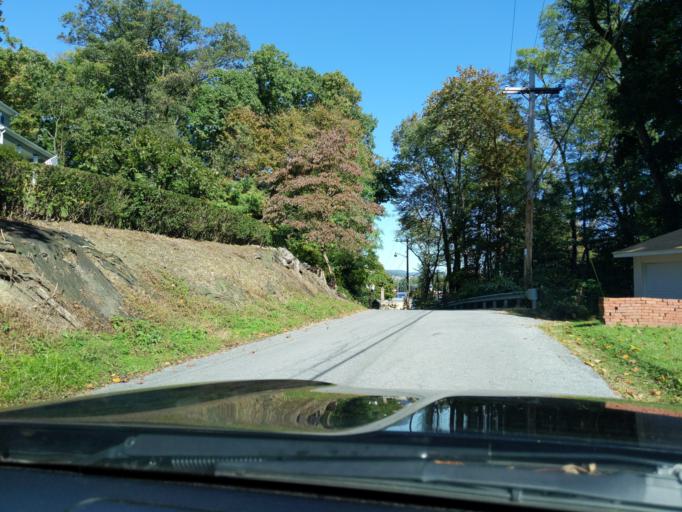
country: US
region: Pennsylvania
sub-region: Blair County
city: Lakemont
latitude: 40.4863
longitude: -78.4096
